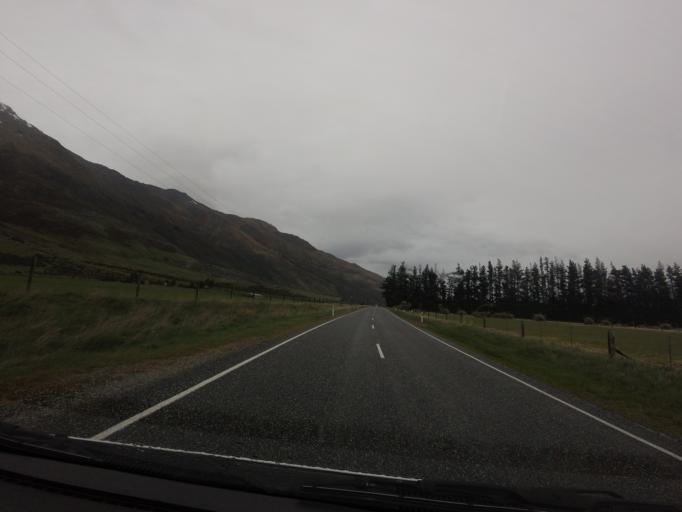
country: NZ
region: Otago
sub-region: Queenstown-Lakes District
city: Wanaka
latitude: -44.2744
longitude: 169.2016
